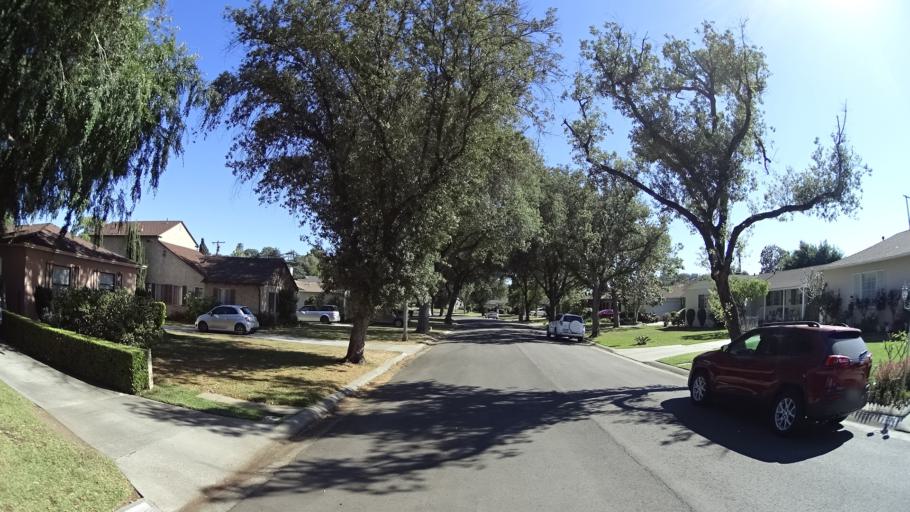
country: US
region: California
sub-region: Los Angeles County
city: Monterey Park
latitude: 34.0684
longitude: -118.1410
